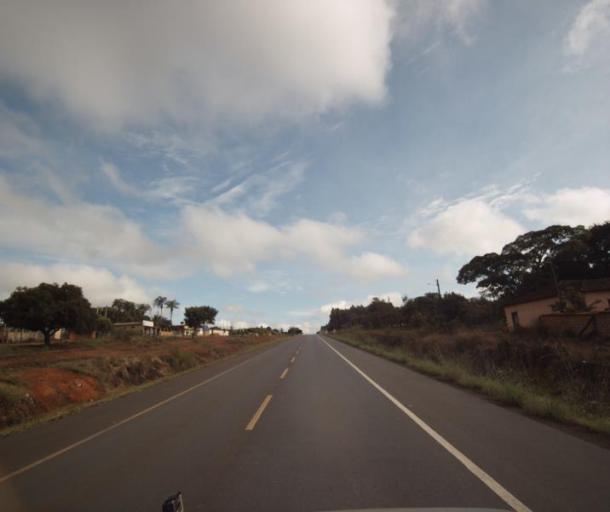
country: BR
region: Goias
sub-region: Barro Alto
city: Barro Alto
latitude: -15.2130
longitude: -48.6987
